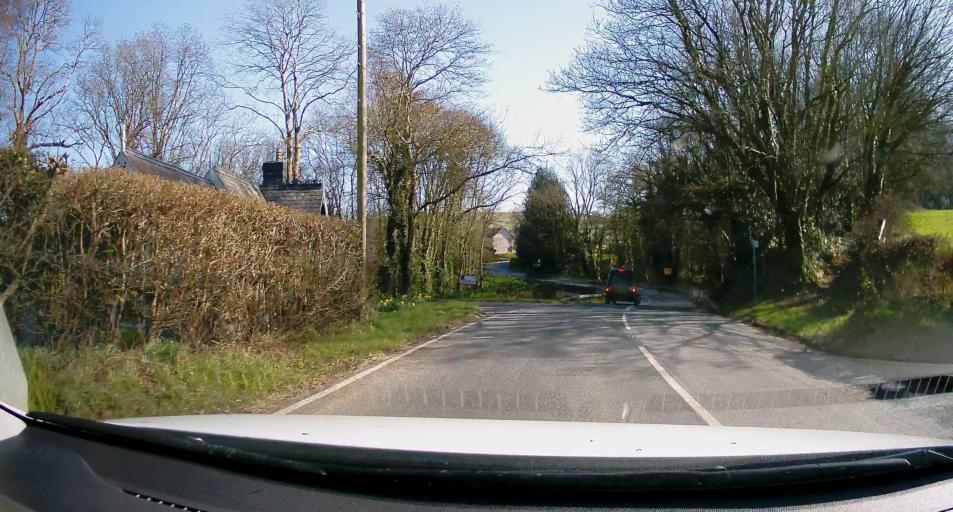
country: GB
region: Wales
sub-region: County of Ceredigion
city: Penparcau
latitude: 52.3629
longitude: -4.0586
